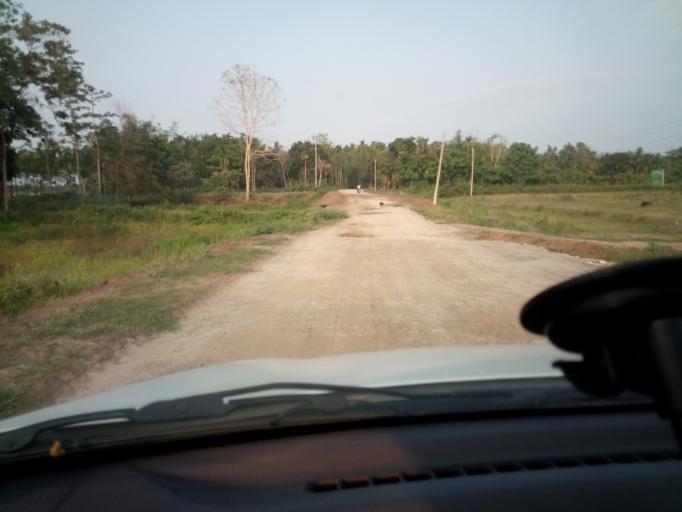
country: IN
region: Assam
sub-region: Udalguri
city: Udalguri
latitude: 26.7081
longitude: 92.0831
